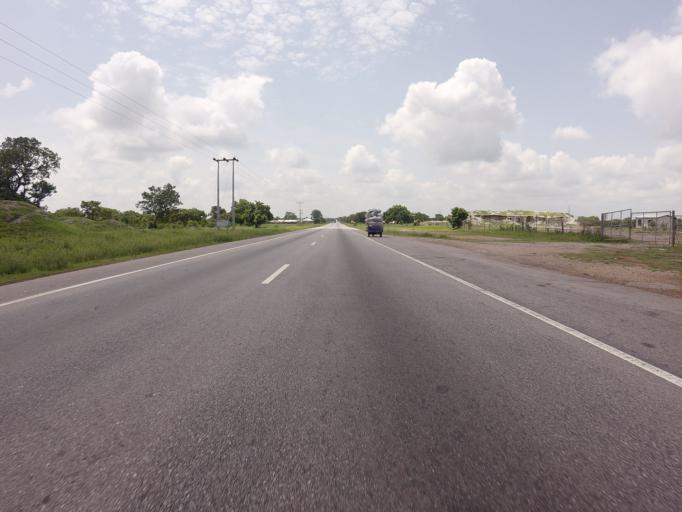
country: GH
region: Northern
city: Tamale
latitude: 9.1295
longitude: -1.2090
